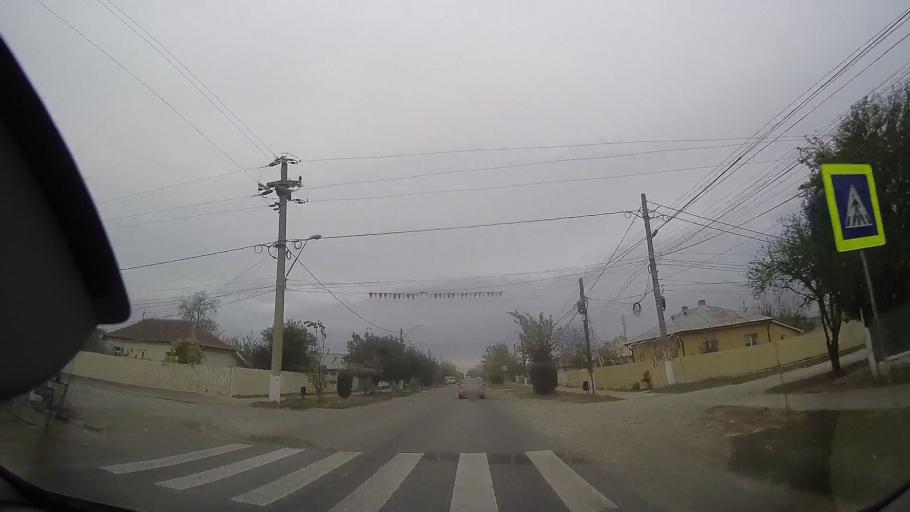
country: RO
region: Ialomita
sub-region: Oras Amara
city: Amara
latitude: 44.6212
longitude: 27.3082
